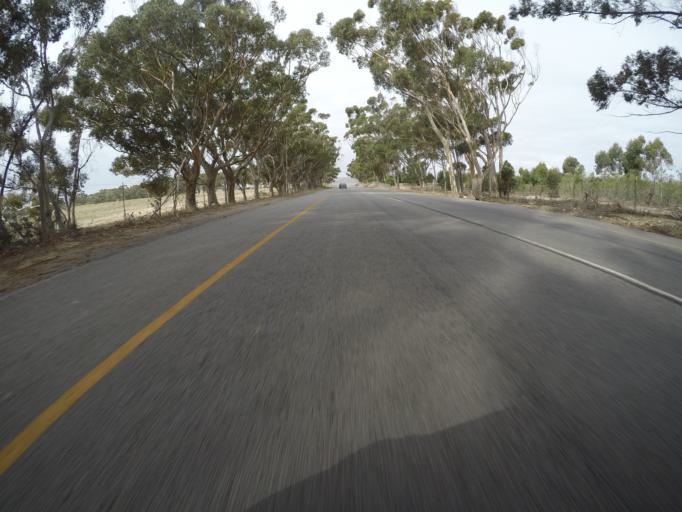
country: ZA
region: Western Cape
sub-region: City of Cape Town
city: Sunset Beach
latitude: -33.7227
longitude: 18.5043
